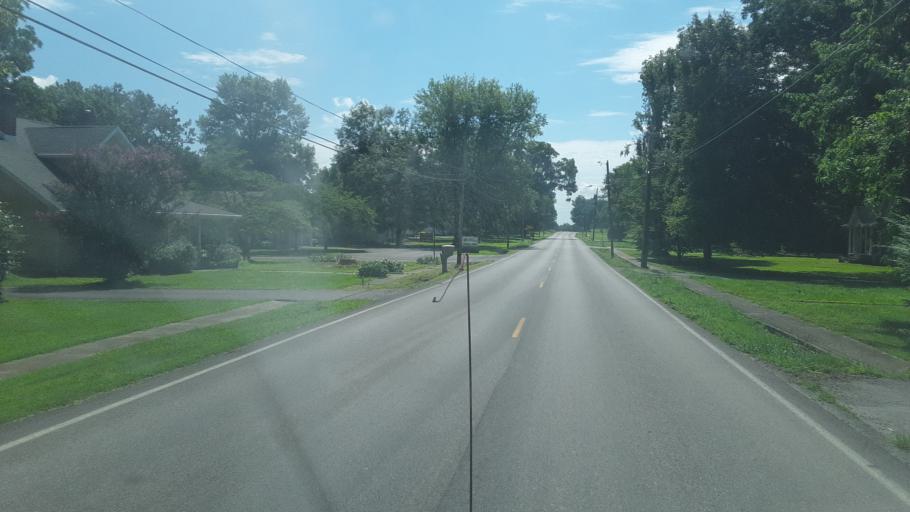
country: US
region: Kentucky
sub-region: Christian County
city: Oak Grove
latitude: 36.7774
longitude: -87.3508
